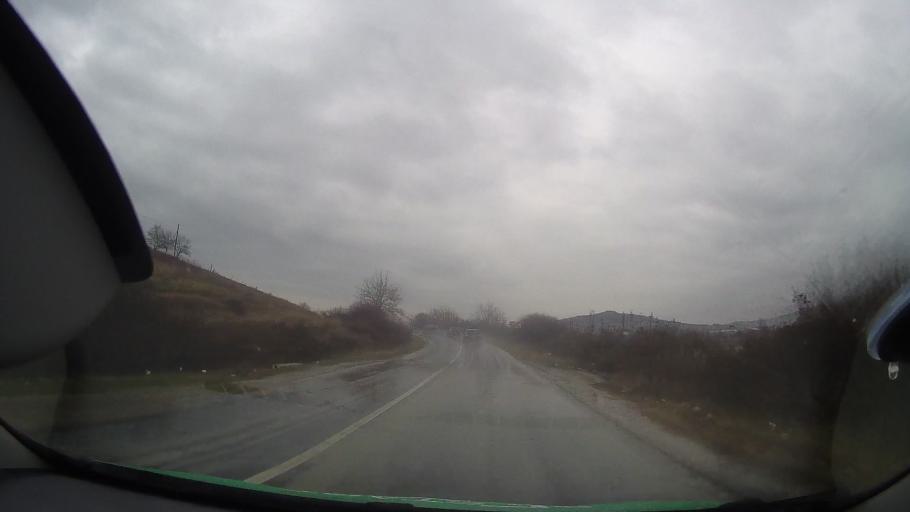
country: RO
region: Bihor
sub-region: Comuna Rabagani
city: Rabagani
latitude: 46.7550
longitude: 22.2062
